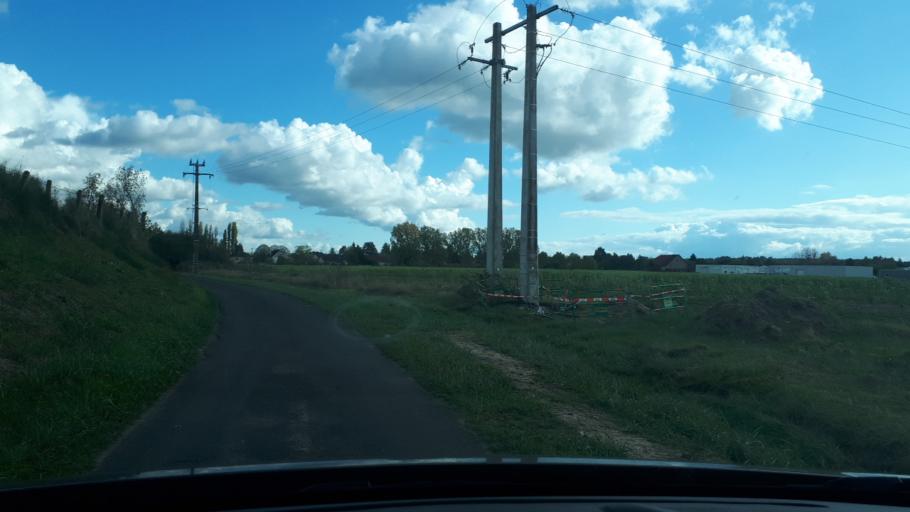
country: FR
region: Centre
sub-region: Departement du Loir-et-Cher
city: Saint-Aignan
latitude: 47.2880
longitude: 1.3799
